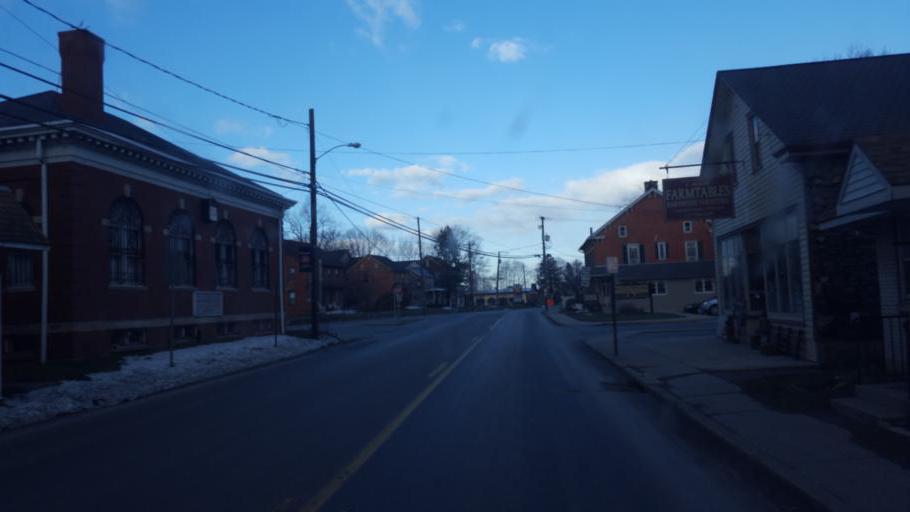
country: US
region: Pennsylvania
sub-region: Lancaster County
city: Intercourse
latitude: 40.0385
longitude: -76.1068
